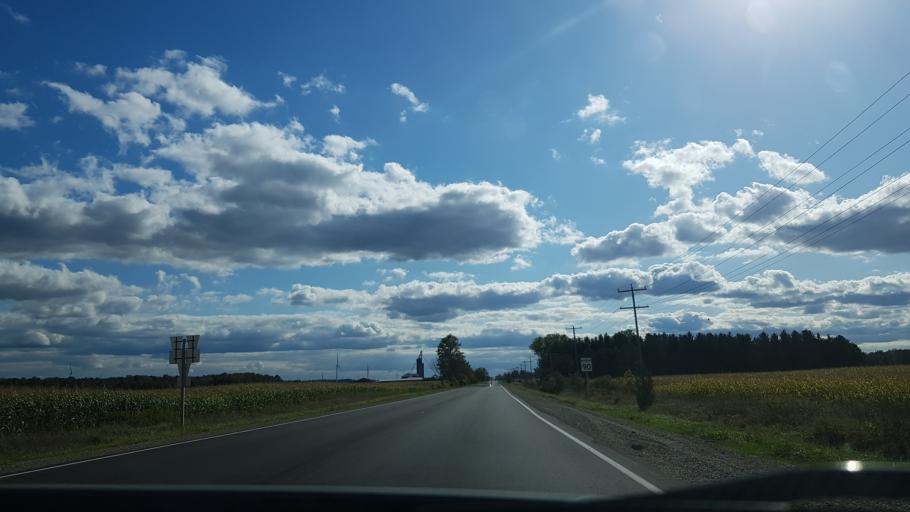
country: CA
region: Ontario
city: South Huron
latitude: 43.1481
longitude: -81.6627
